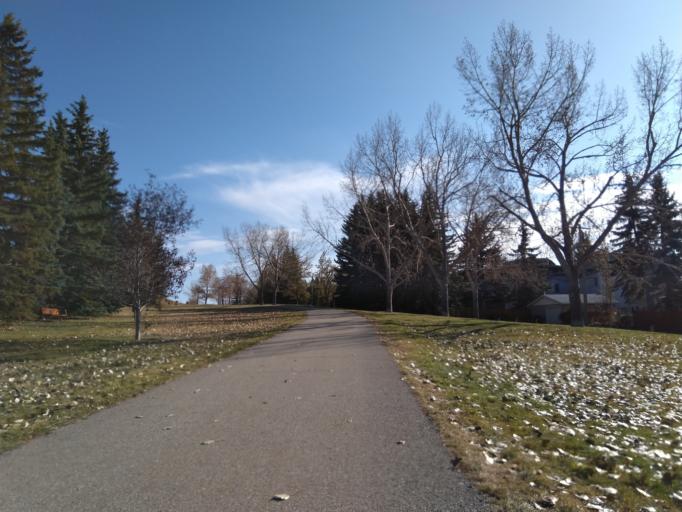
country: CA
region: Alberta
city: Calgary
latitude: 51.1018
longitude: -114.1262
